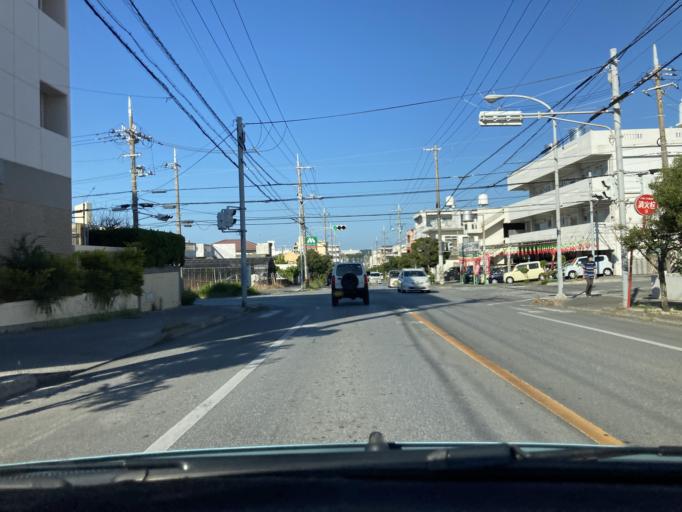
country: JP
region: Okinawa
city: Ginowan
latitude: 26.2811
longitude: 127.7816
